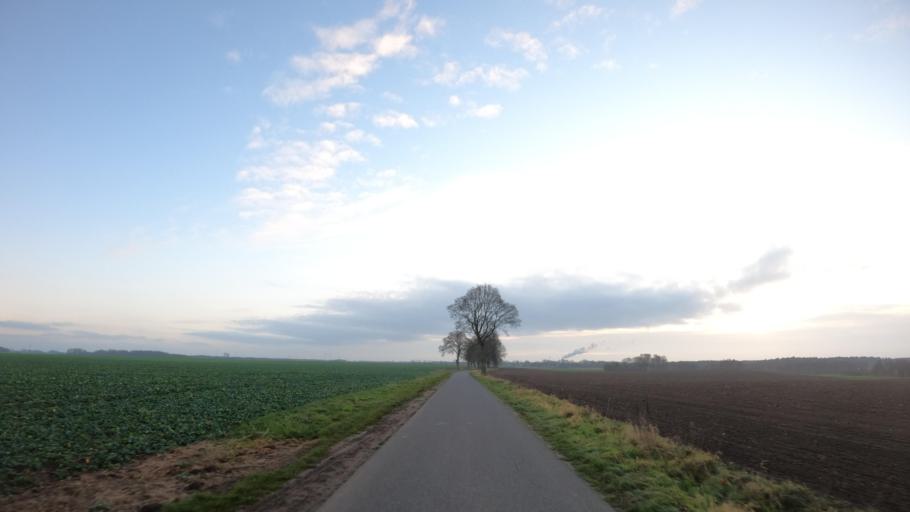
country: PL
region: West Pomeranian Voivodeship
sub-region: Powiat bialogardzki
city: Karlino
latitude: 54.0936
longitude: 15.8863
